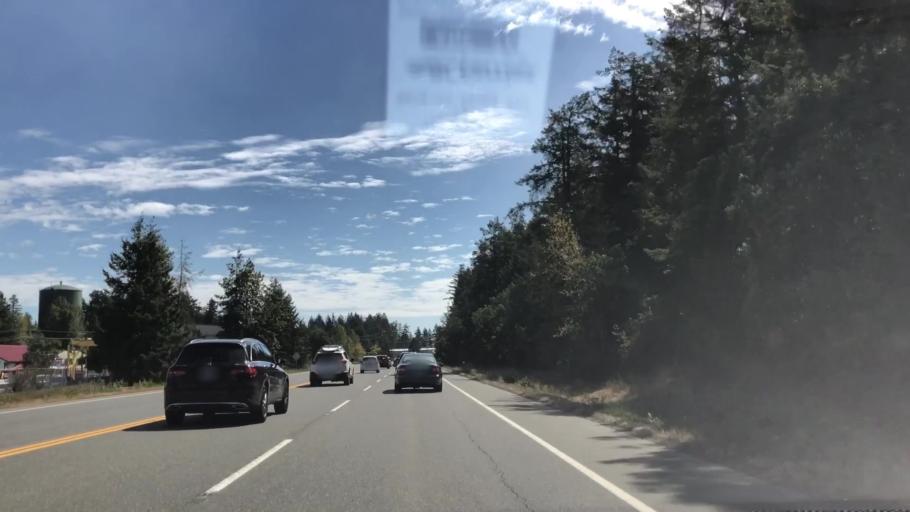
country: CA
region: British Columbia
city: Nanaimo
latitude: 49.1358
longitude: -123.8742
